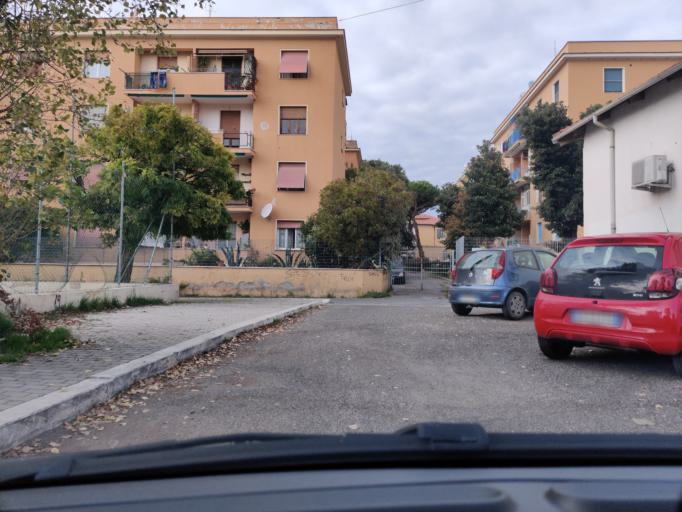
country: IT
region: Latium
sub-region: Citta metropolitana di Roma Capitale
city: Civitavecchia
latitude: 42.0952
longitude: 11.7990
